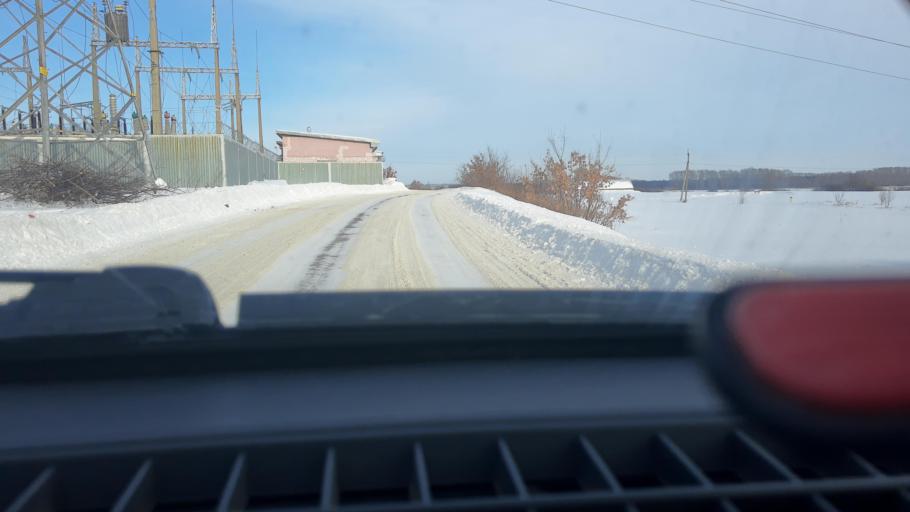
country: RU
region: Bashkortostan
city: Ufa
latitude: 54.5304
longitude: 55.9121
